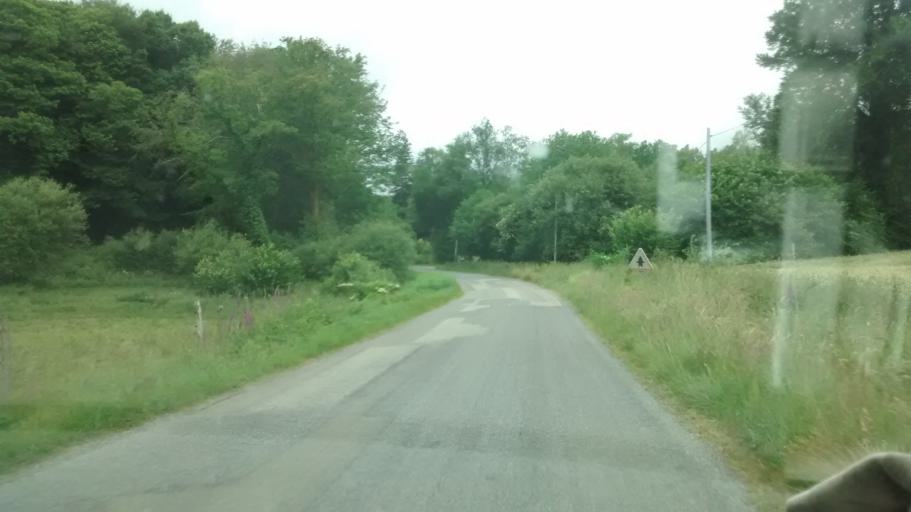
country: FR
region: Brittany
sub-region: Departement du Morbihan
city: Molac
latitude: 47.7203
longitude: -2.4651
